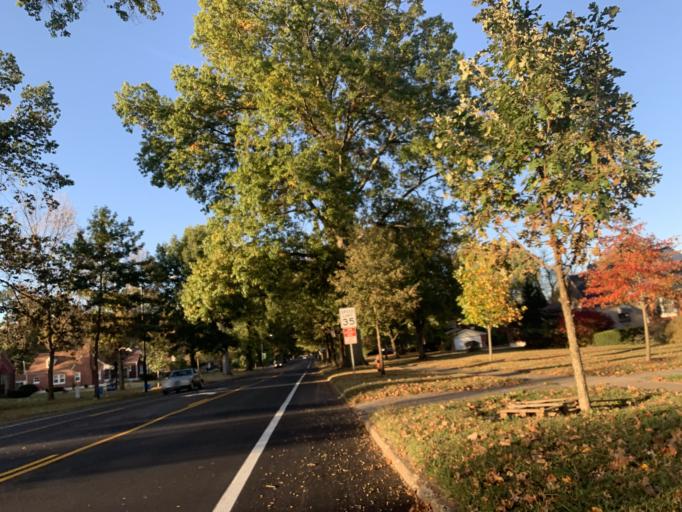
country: US
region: Indiana
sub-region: Floyd County
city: New Albany
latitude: 38.2459
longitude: -85.8298
